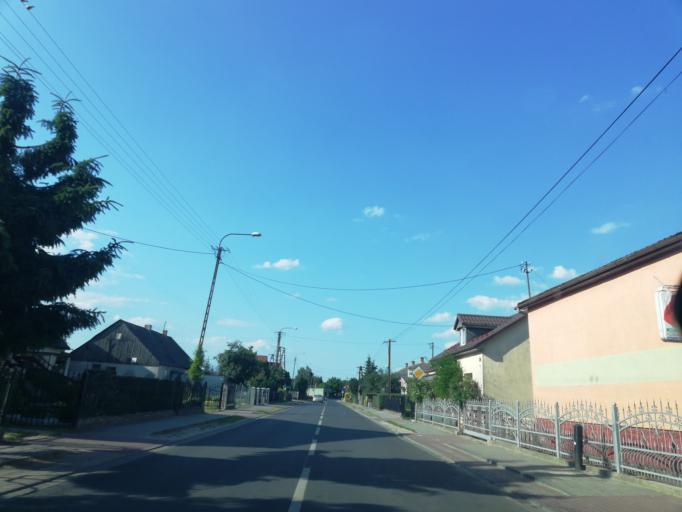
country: PL
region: Kujawsko-Pomorskie
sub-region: Powiat golubsko-dobrzynski
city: Golub-Dobrzyn
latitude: 53.0144
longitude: 19.0549
